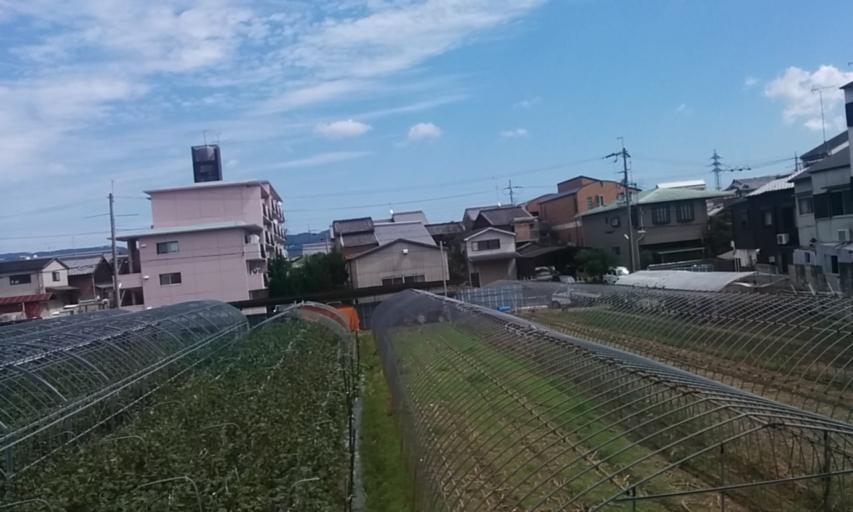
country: JP
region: Kyoto
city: Uji
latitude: 34.9220
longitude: 135.7671
